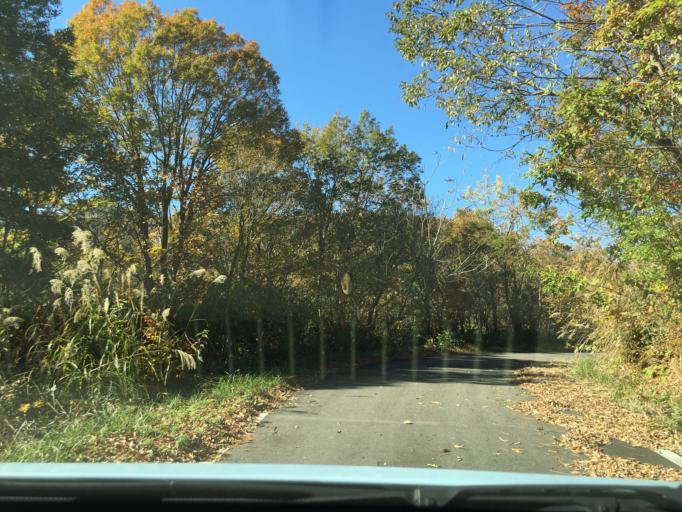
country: JP
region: Fukushima
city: Inawashiro
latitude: 37.3943
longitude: 140.0217
